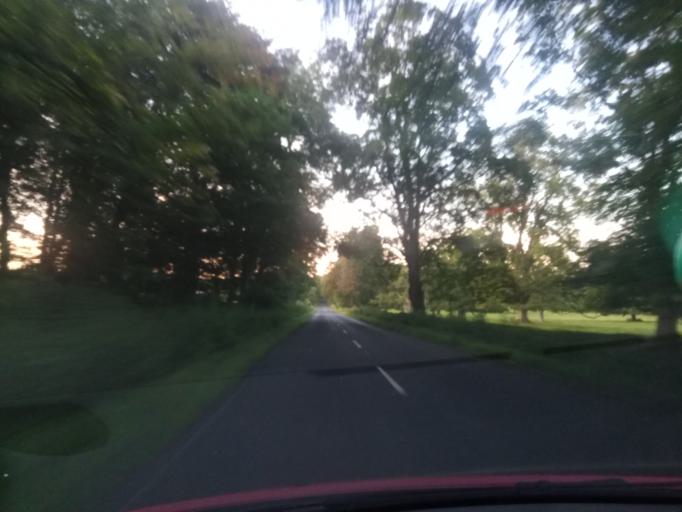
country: GB
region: England
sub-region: Northumberland
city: Bardon Mill
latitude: 54.8954
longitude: -2.3517
